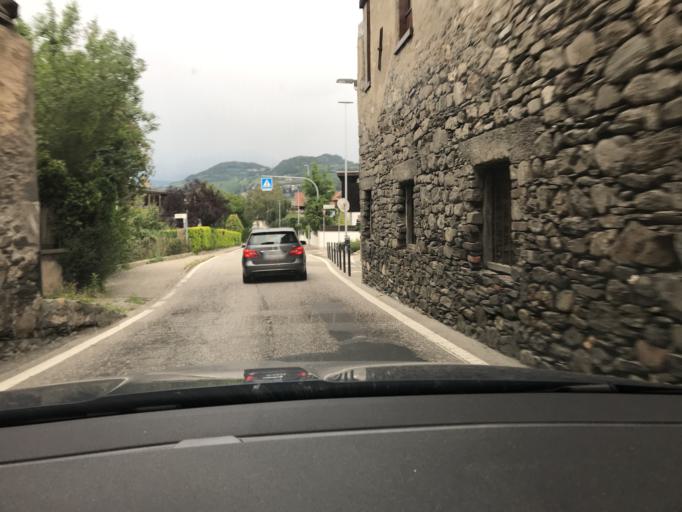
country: IT
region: Trentino-Alto Adige
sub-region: Bolzano
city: Bressanone
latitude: 46.7039
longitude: 11.6599
